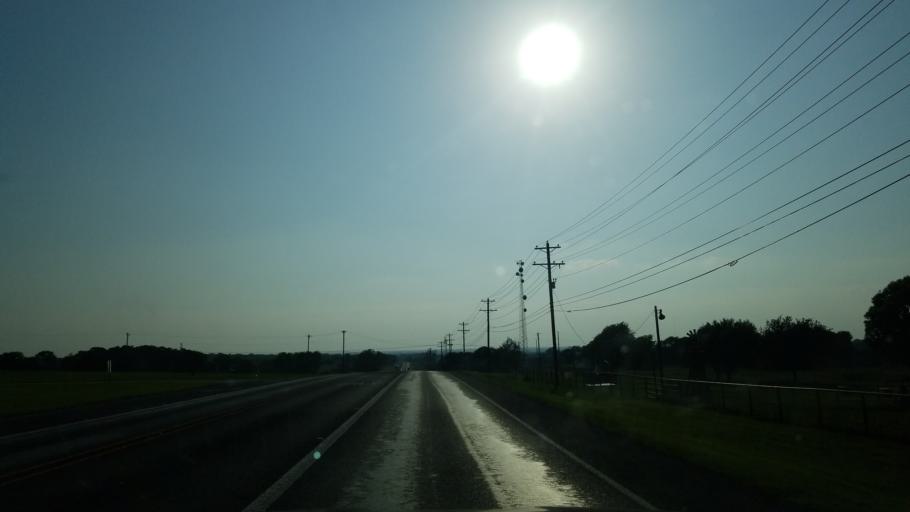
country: US
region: Texas
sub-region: Denton County
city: Aubrey
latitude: 33.3045
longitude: -96.9954
